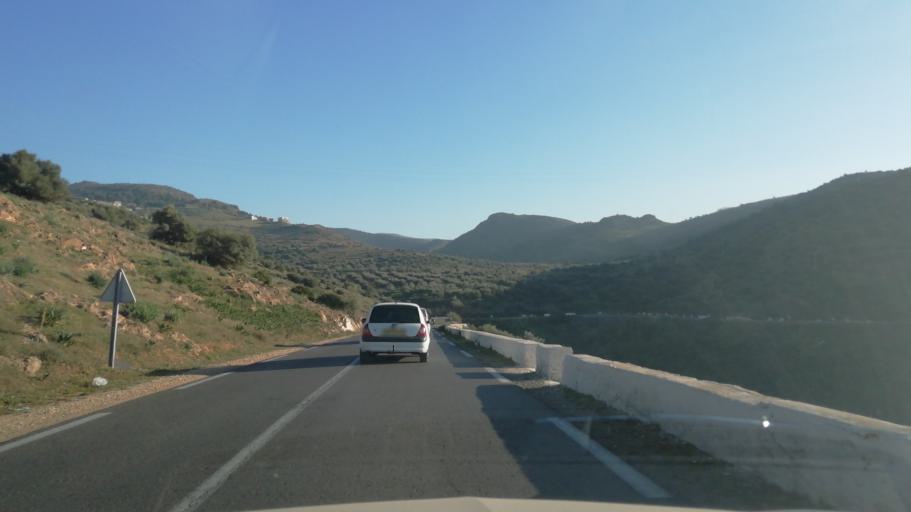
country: DZ
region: Tlemcen
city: Beni Mester
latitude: 34.8520
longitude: -1.4518
